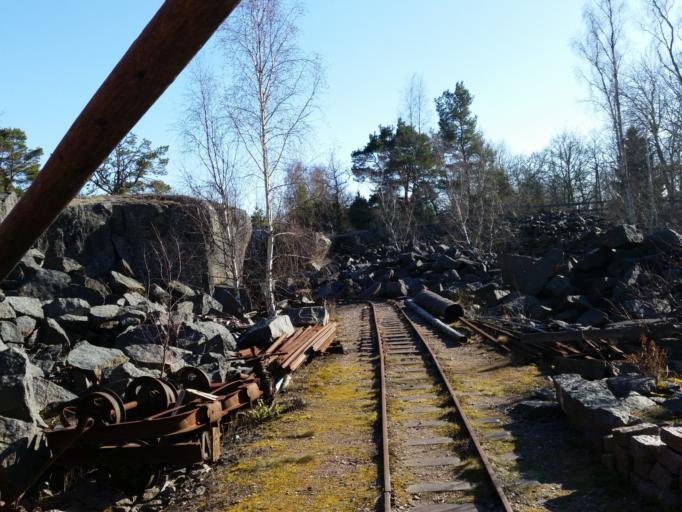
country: SE
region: Kalmar
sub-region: Oskarshamns Kommun
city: Paskallavik
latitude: 57.1856
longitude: 16.4523
